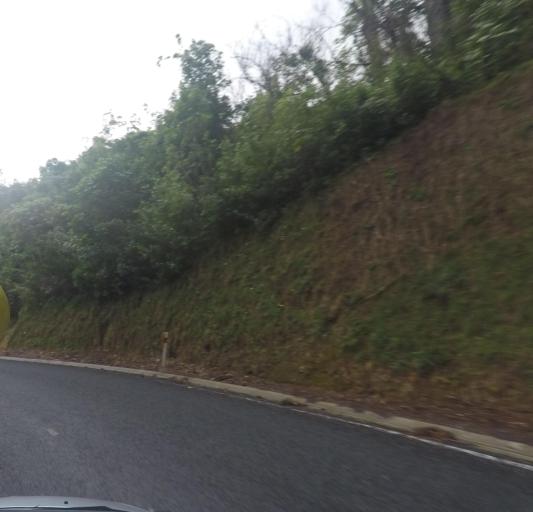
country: NZ
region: Auckland
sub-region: Auckland
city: Warkworth
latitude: -36.3747
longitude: 174.8056
